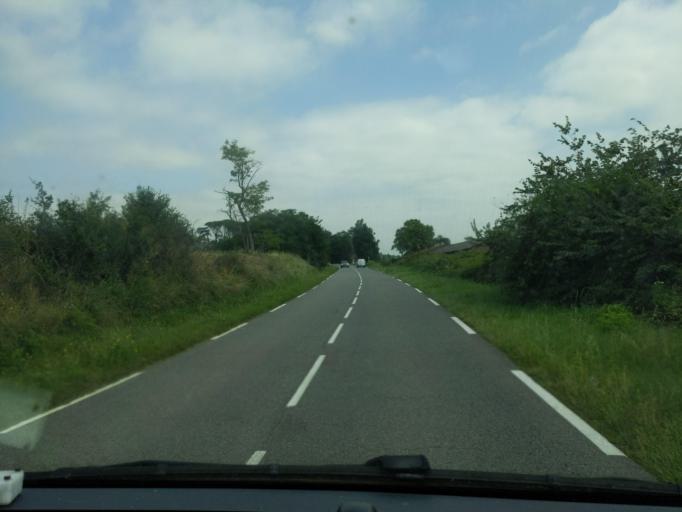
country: FR
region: Midi-Pyrenees
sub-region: Departement de la Haute-Garonne
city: Saint-Orens-de-Gameville
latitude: 43.5673
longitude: 1.5310
